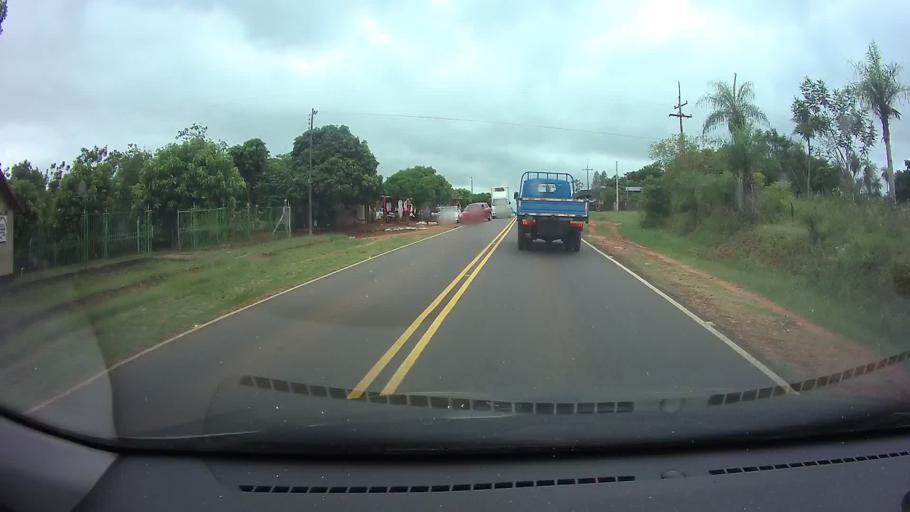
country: PY
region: Paraguari
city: Carapegua
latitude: -25.7261
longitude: -57.3174
